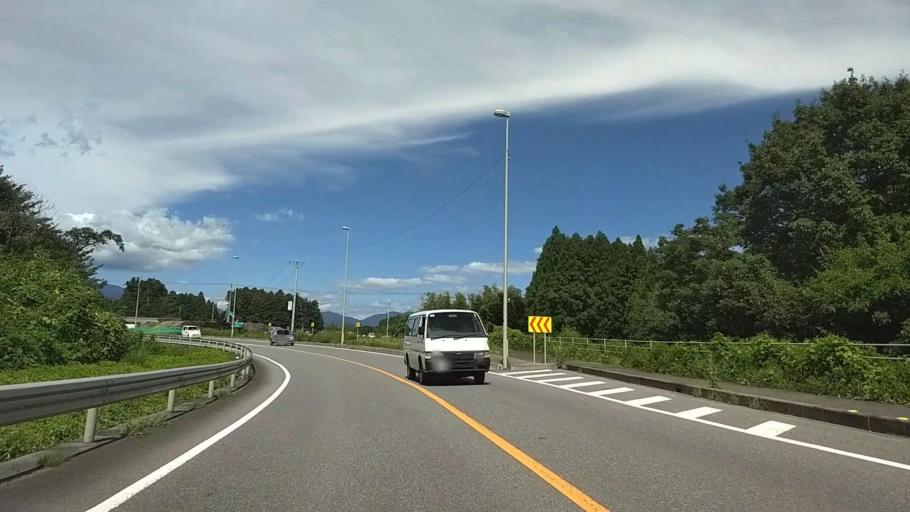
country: JP
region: Tochigi
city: Imaichi
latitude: 36.7057
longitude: 139.7486
